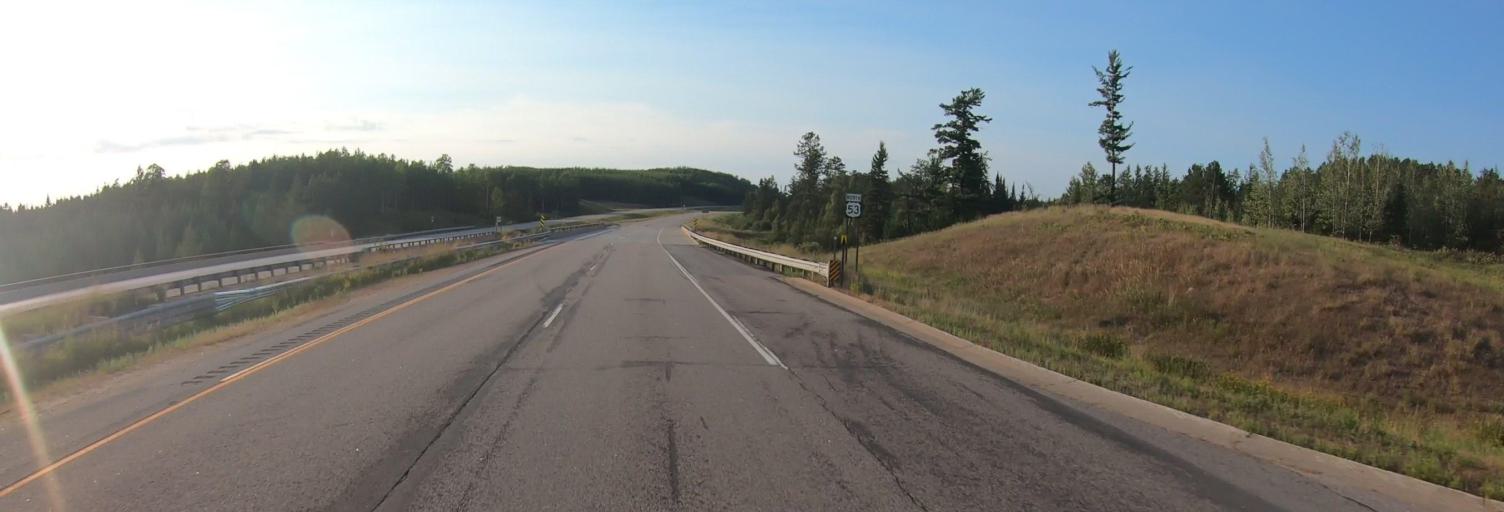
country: US
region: Minnesota
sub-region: Saint Louis County
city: Mountain Iron
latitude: 47.6775
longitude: -92.6353
